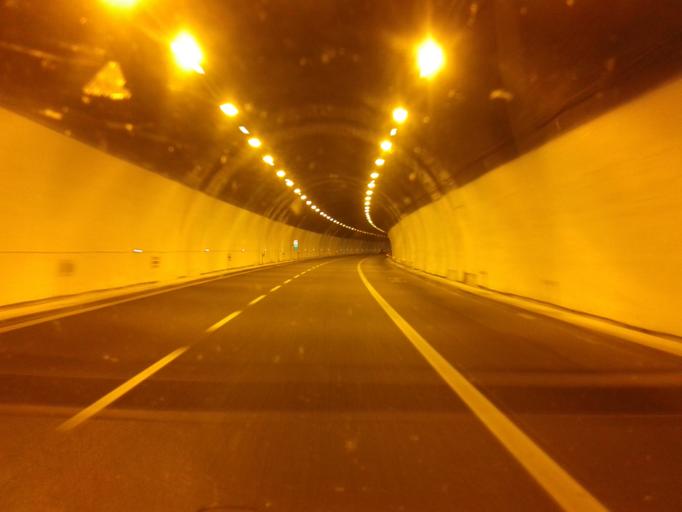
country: IT
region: Friuli Venezia Giulia
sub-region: Provincia di Udine
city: Bordano
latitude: 46.3372
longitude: 13.0710
